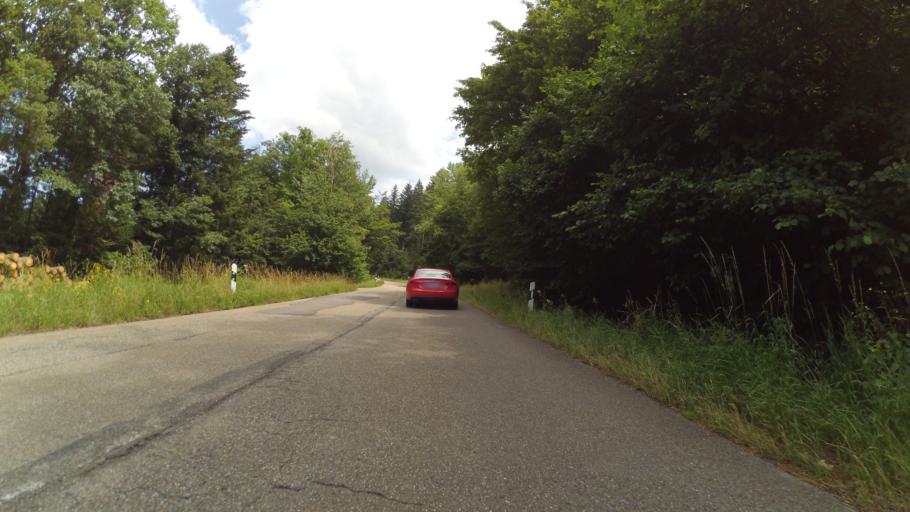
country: DE
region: Baden-Wuerttemberg
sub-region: Freiburg Region
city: Badenweiler
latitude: 47.7935
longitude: 7.6731
